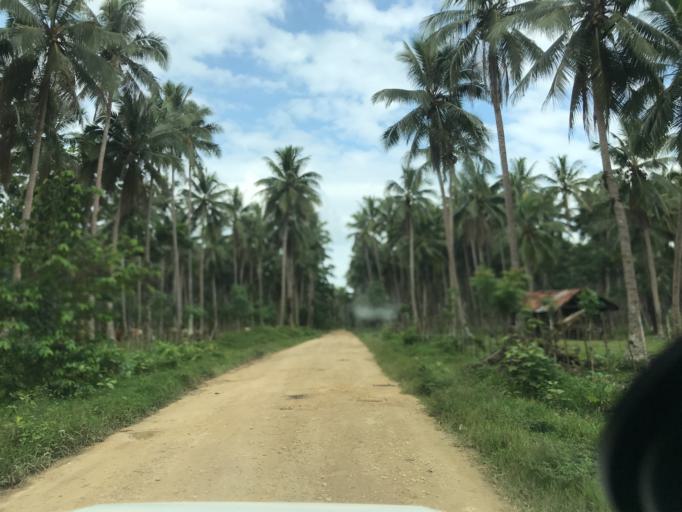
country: VU
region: Sanma
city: Port-Olry
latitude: -15.1872
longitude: 167.0617
